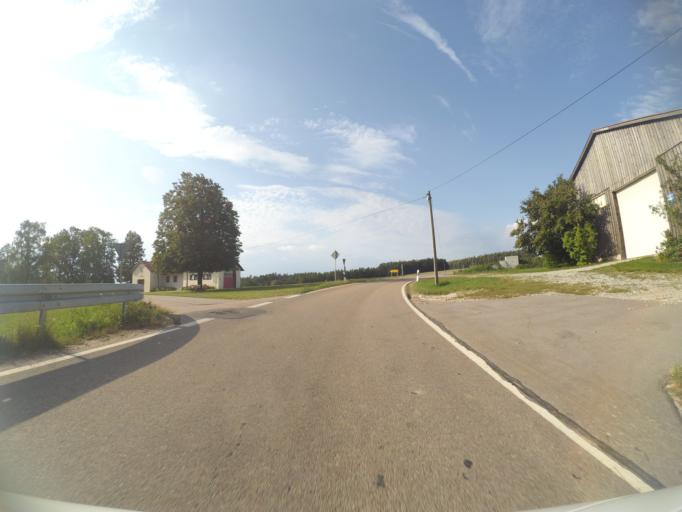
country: DE
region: Bavaria
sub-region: Upper Palatinate
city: Stulln
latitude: 49.4586
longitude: 12.1244
